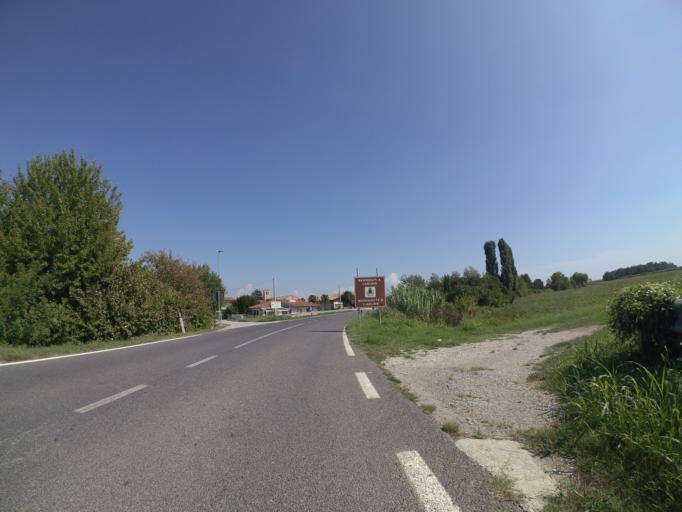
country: IT
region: Friuli Venezia Giulia
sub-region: Provincia di Udine
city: Muzzana del Turgnano
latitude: 45.8125
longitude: 13.1581
